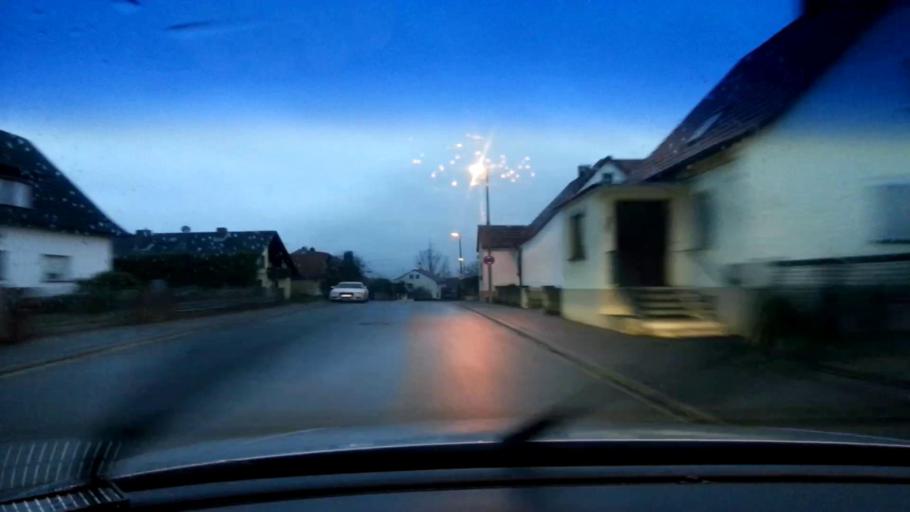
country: DE
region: Bavaria
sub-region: Upper Franconia
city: Memmelsdorf
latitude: 49.9563
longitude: 10.9567
